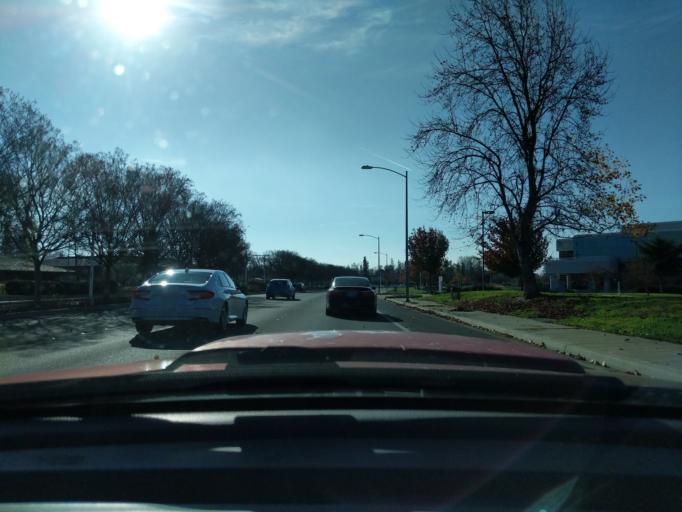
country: US
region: California
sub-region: Santa Clara County
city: Milpitas
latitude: 37.4131
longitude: -121.9181
